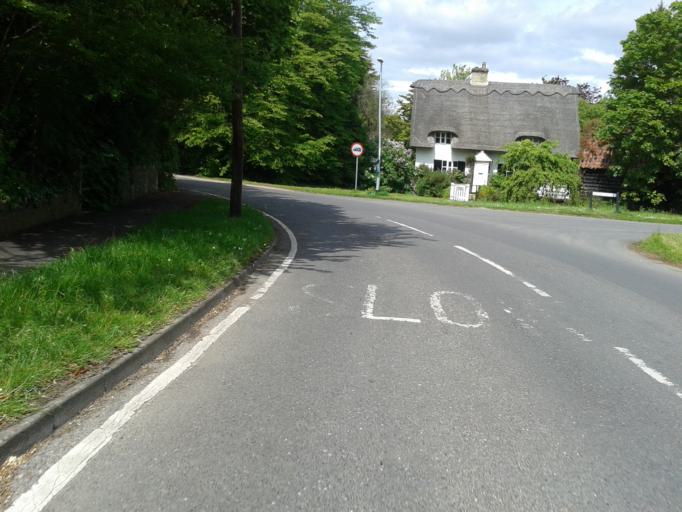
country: GB
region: England
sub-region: Cambridgeshire
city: Meldreth
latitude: 52.1121
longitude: 0.0348
